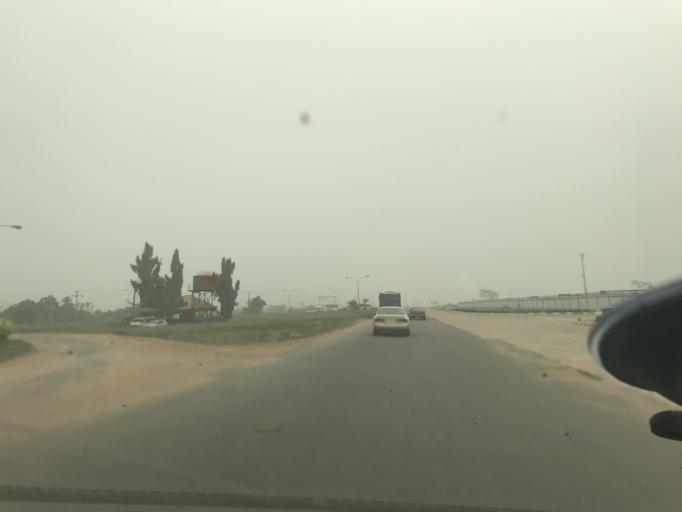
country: NG
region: Ogun
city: Owode
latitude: 6.8892
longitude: 3.5688
